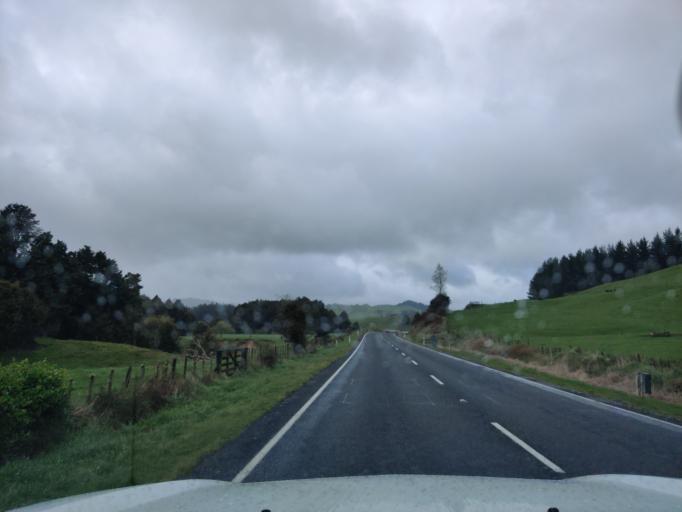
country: NZ
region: Waikato
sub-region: Otorohanga District
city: Otorohanga
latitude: -38.6900
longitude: 175.2125
